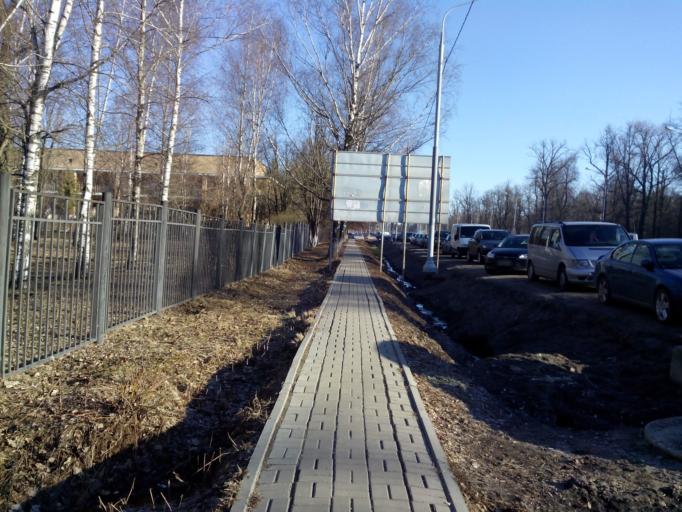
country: RU
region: Moskovskaya
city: Odintsovo
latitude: 55.6839
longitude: 37.2716
